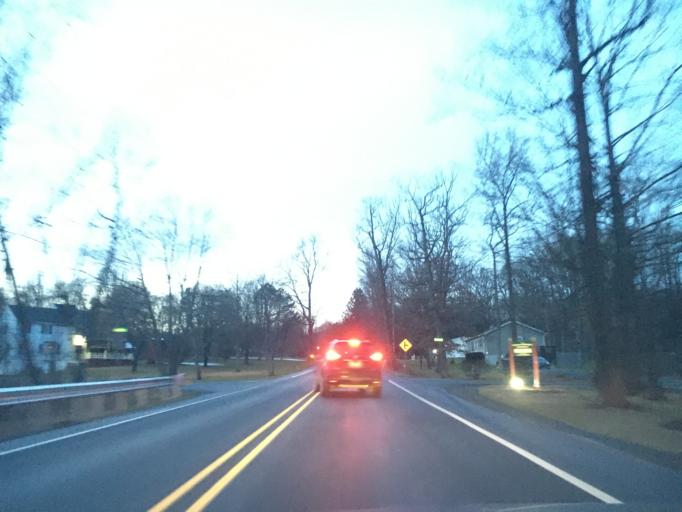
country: US
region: Pennsylvania
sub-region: Northampton County
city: Cherryville
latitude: 40.7495
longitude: -75.5234
